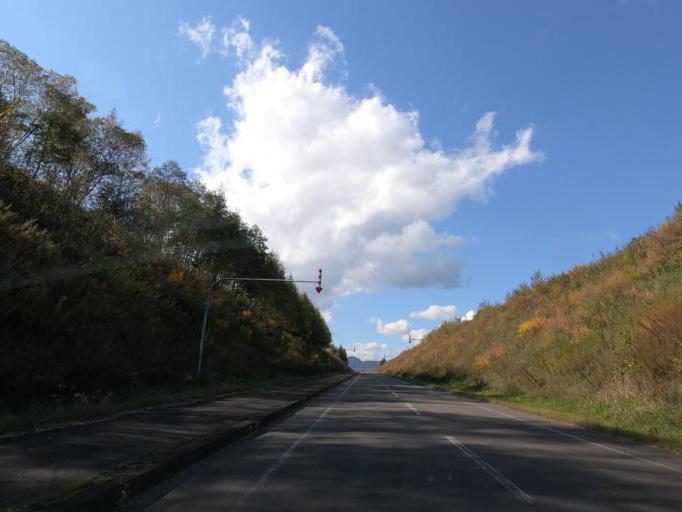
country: JP
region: Hokkaido
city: Otofuke
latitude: 43.2399
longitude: 143.2638
